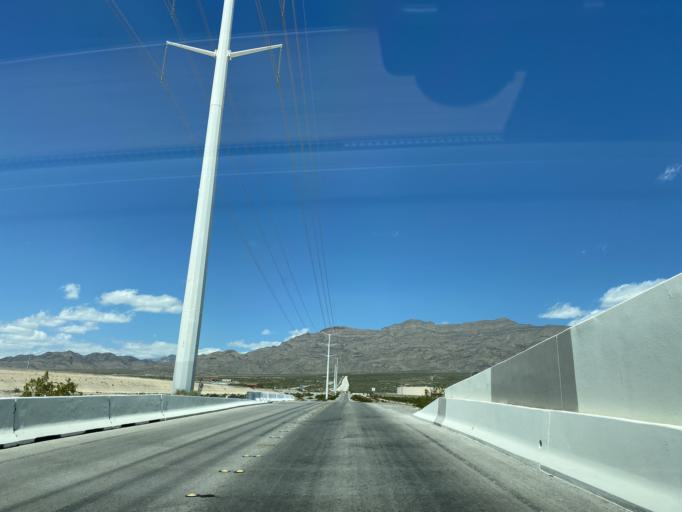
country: US
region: Nevada
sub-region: Clark County
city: North Las Vegas
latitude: 36.3290
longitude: -115.2071
